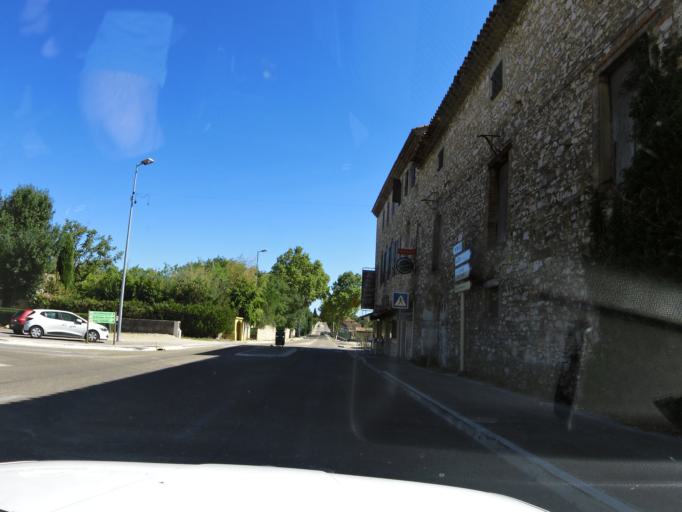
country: FR
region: Languedoc-Roussillon
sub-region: Departement du Gard
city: Vezenobres
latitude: 44.0498
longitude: 4.1404
